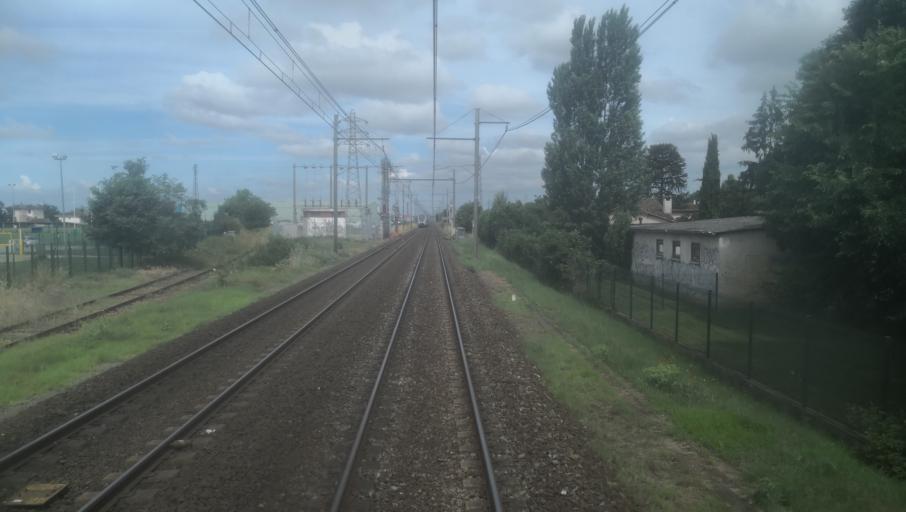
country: FR
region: Aquitaine
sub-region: Departement du Lot-et-Garonne
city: Marmande
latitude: 44.5088
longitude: 0.1561
